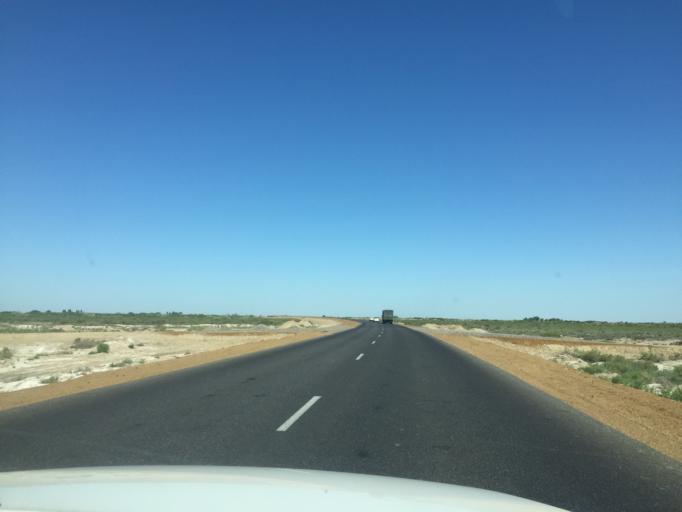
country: KZ
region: Qyzylorda
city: Dzhalagash
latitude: 44.8791
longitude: 64.7938
